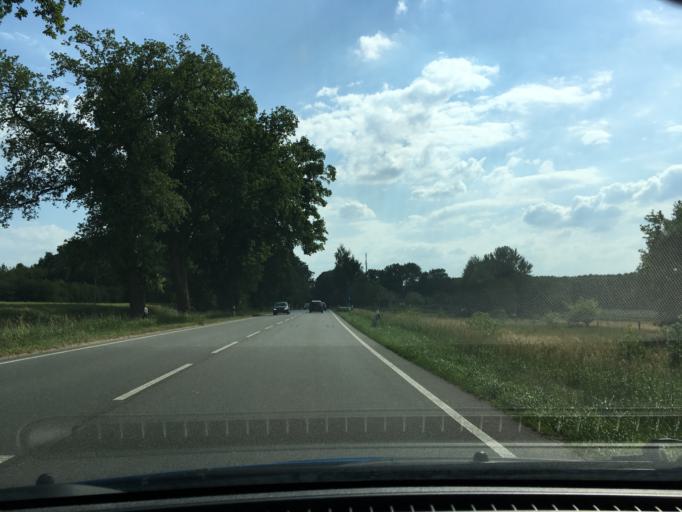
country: DE
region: Lower Saxony
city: Welle
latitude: 53.2478
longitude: 9.8078
